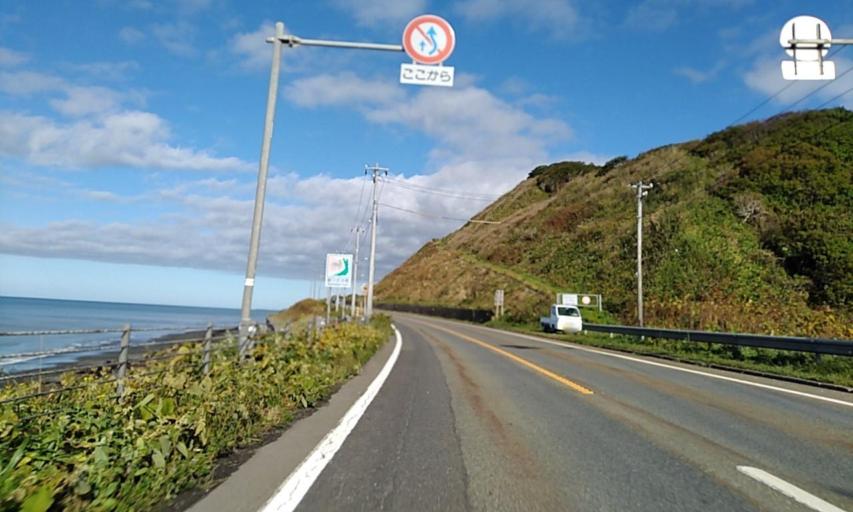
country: JP
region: Hokkaido
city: Shizunai-furukawacho
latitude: 42.2089
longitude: 142.6499
